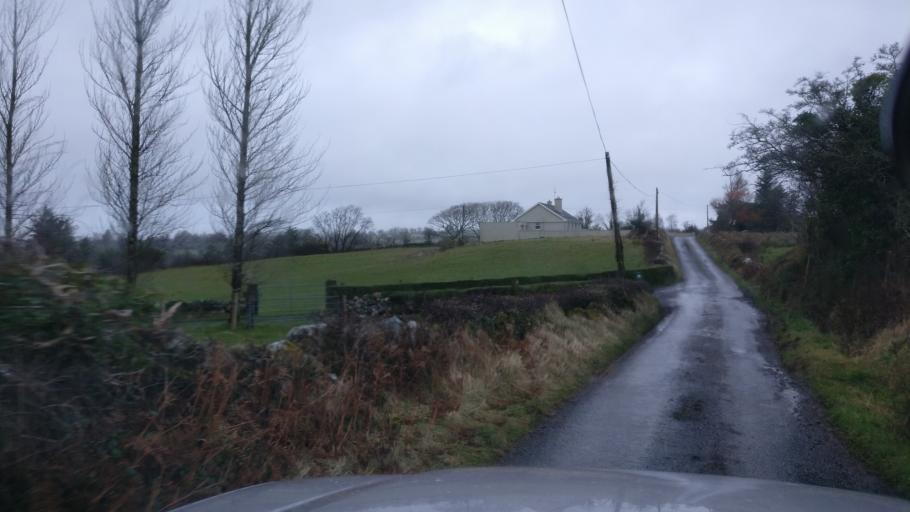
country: IE
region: Connaught
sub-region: County Galway
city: Loughrea
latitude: 53.1516
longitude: -8.6138
